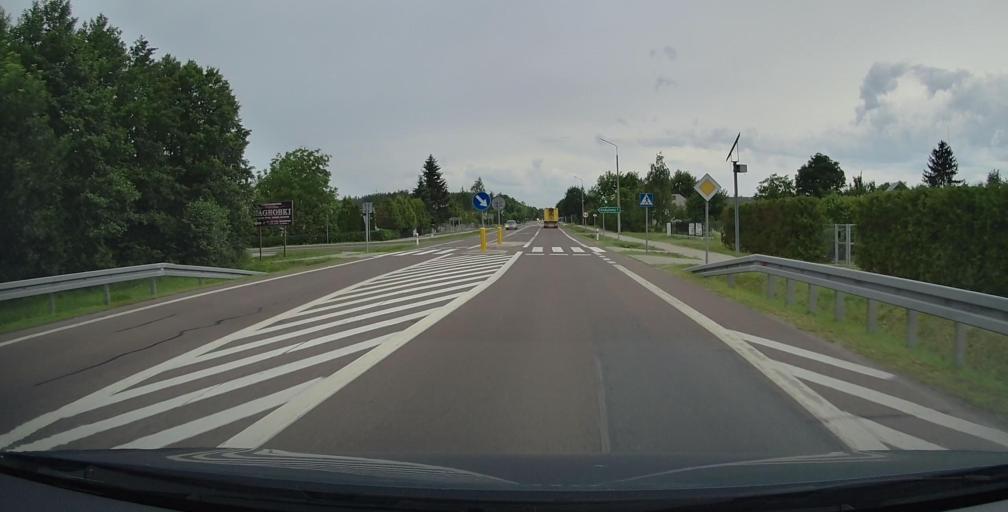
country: PL
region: Lublin Voivodeship
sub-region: Powiat bialski
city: Terespol
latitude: 52.0484
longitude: 23.5488
